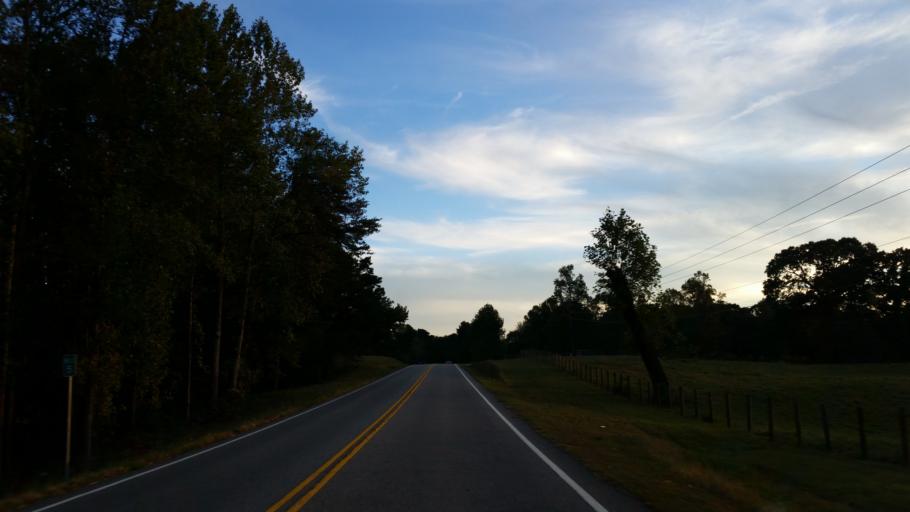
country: US
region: Georgia
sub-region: Dawson County
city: Dawsonville
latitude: 34.3990
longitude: -84.1222
